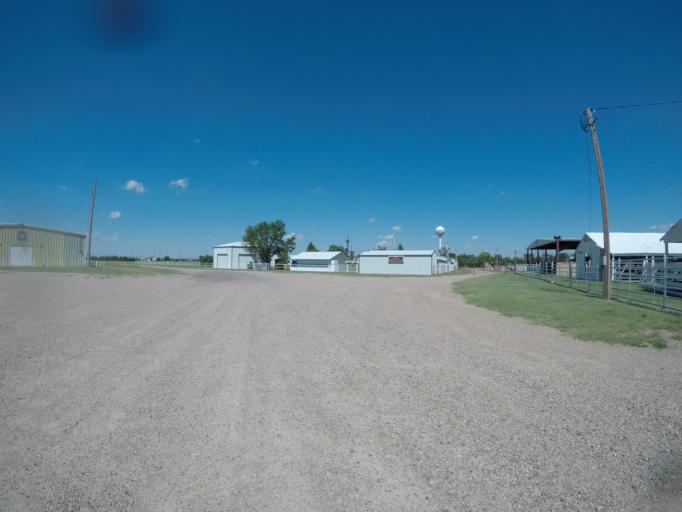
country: US
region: Kansas
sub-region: Sheridan County
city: Hoxie
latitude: 39.3590
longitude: -100.4408
